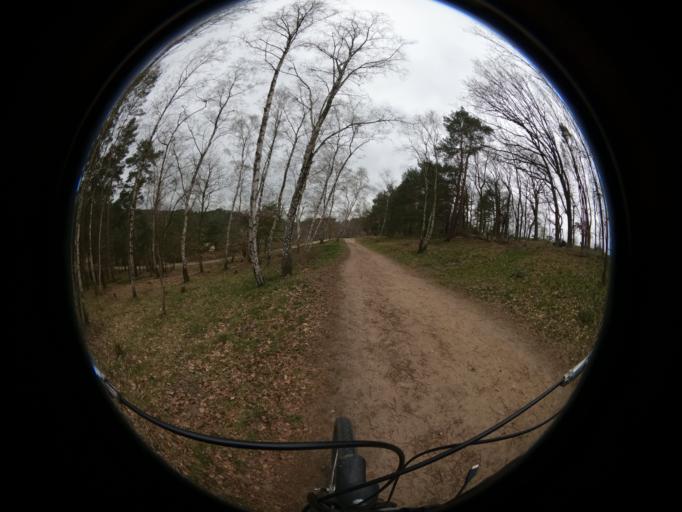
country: DE
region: Lower Saxony
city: Neu Wulmstorf
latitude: 53.4633
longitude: 9.8464
